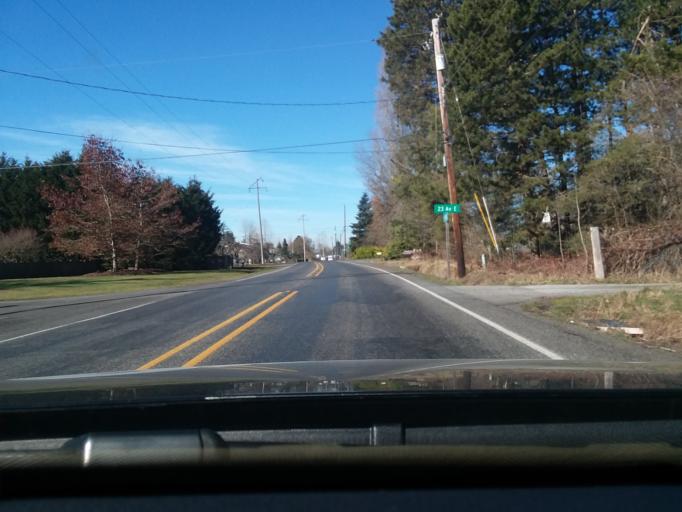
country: US
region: Washington
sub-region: Pierce County
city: Midland
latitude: 47.1623
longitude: -122.3986
